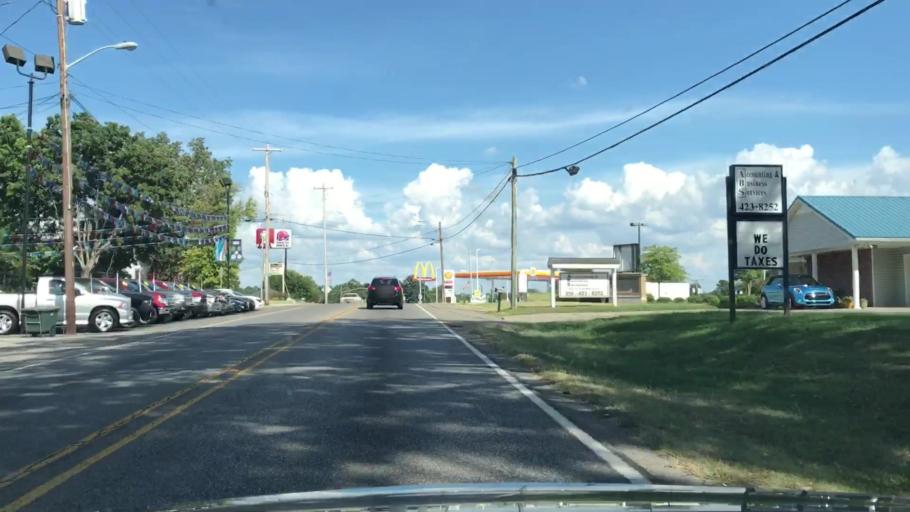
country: US
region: Tennessee
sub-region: Giles County
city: Ardmore
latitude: 34.9919
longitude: -86.8428
